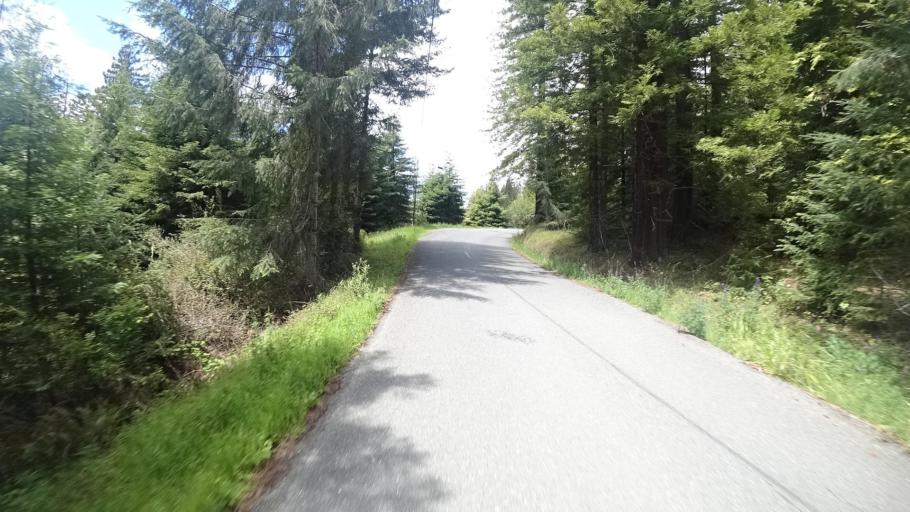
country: US
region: California
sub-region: Humboldt County
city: Blue Lake
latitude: 40.8472
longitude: -123.9253
